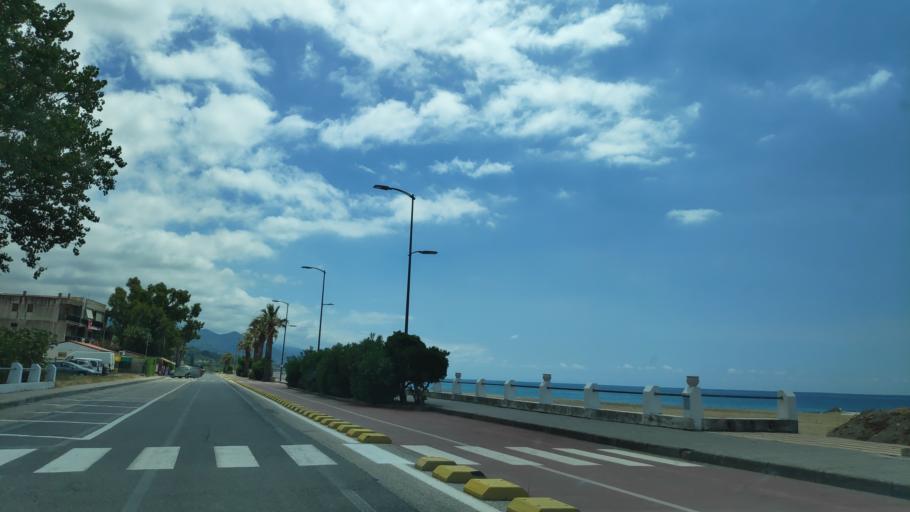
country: IT
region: Calabria
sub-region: Provincia di Cosenza
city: Paola
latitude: 39.3571
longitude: 16.0324
